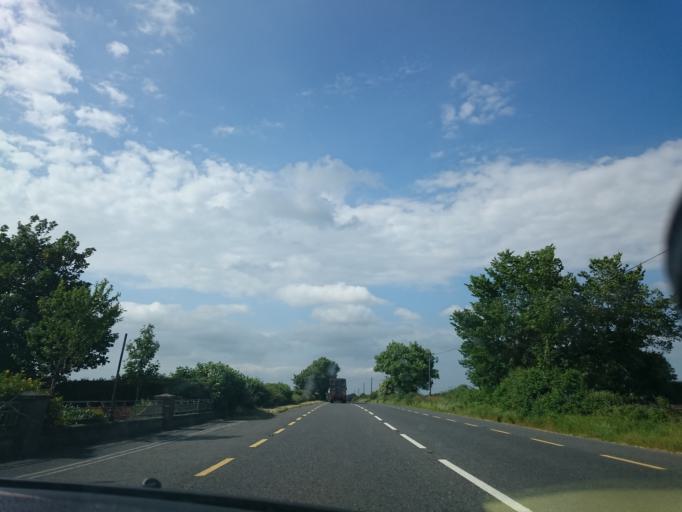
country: IE
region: Leinster
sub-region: Kilkenny
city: Kilkenny
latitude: 52.6129
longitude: -7.2456
